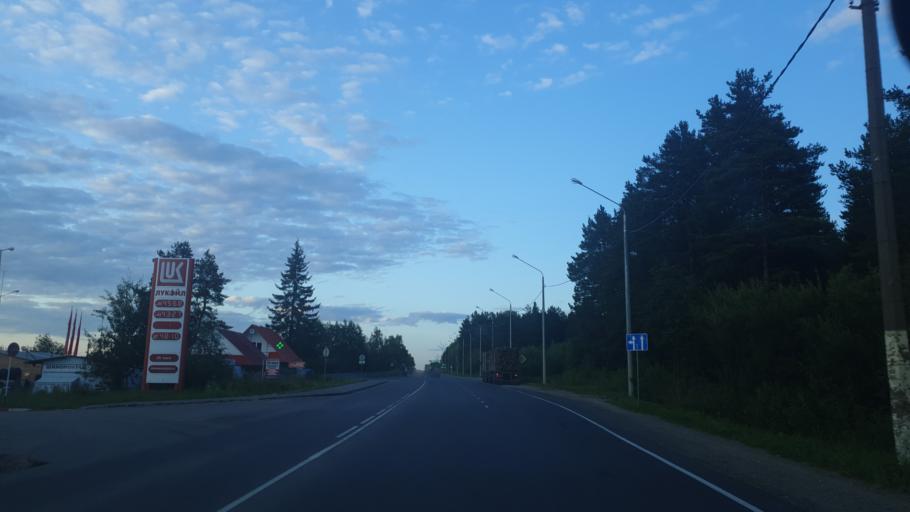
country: RU
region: Komi Republic
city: Verkhnyaya Maksakovka
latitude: 61.6639
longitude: 50.9690
